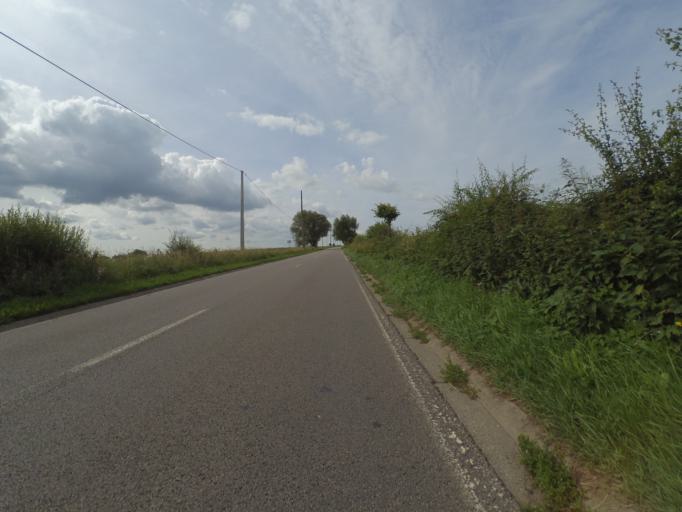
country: BE
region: Wallonia
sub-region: Province de Liege
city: Eupen
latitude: 50.6633
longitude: 6.0423
